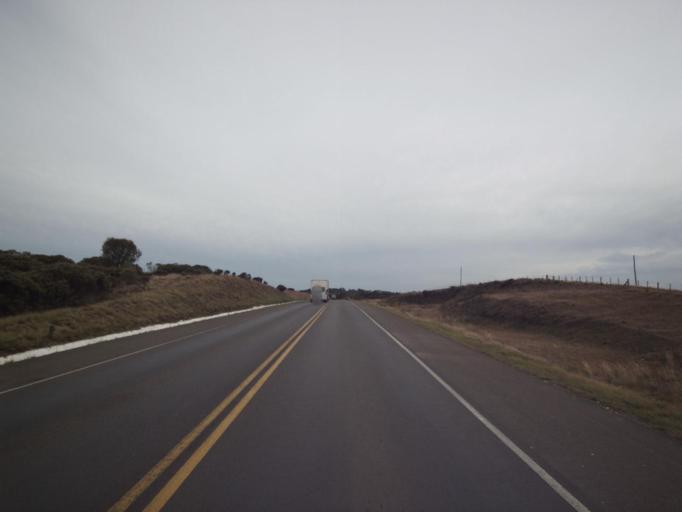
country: BR
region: Parana
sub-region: Palmas
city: Palmas
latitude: -26.6325
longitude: -51.5058
